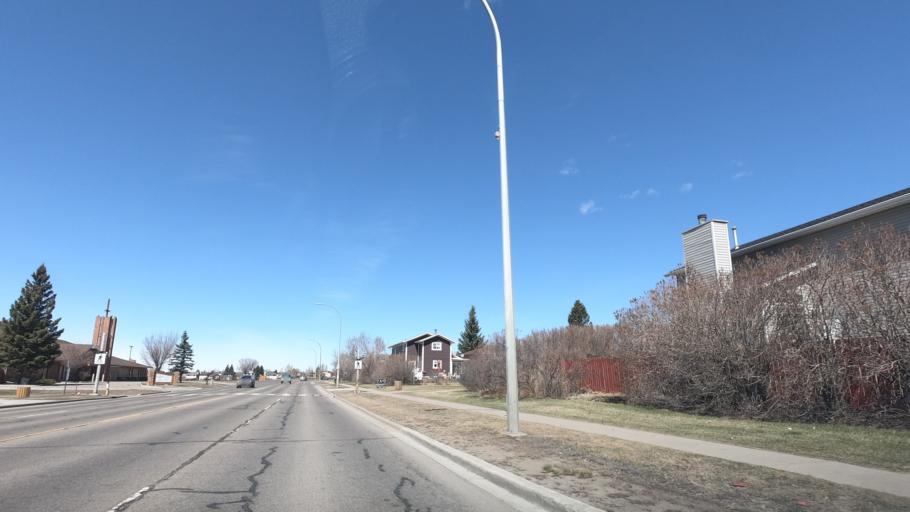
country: CA
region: Alberta
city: Airdrie
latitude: 51.2808
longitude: -114.0090
